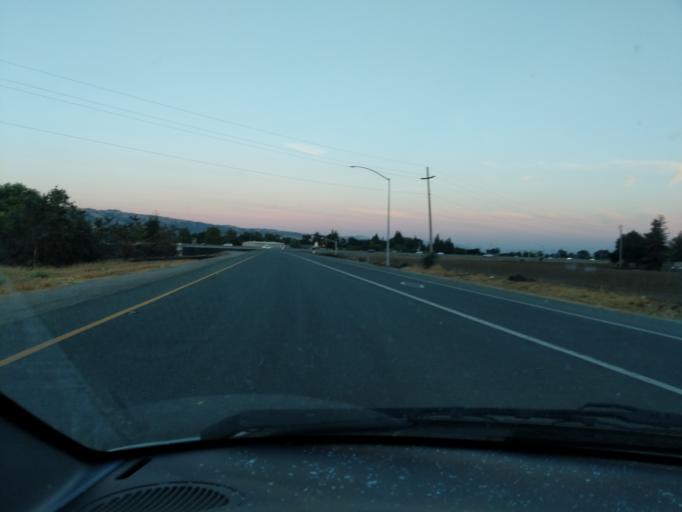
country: US
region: California
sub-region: Santa Clara County
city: San Martin
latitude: 37.0583
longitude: -121.5865
